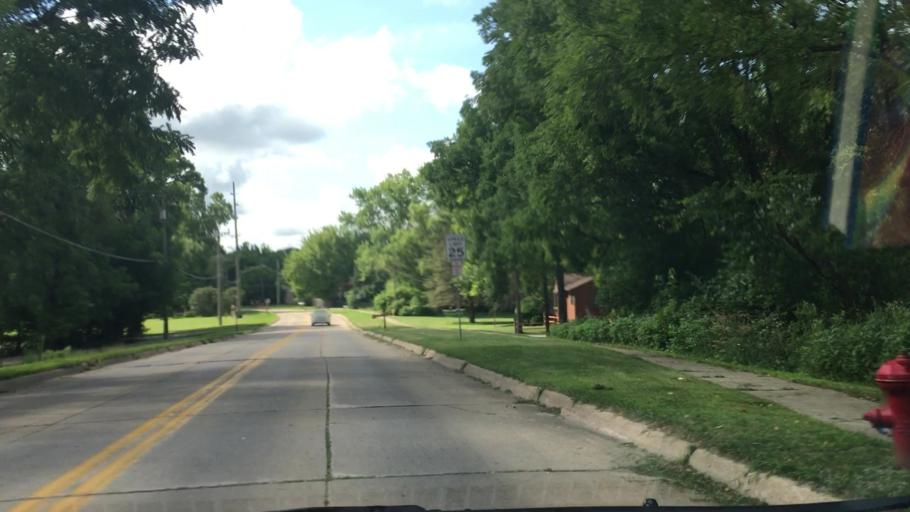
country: US
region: Iowa
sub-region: Johnson County
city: Iowa City
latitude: 41.6869
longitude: -91.5244
